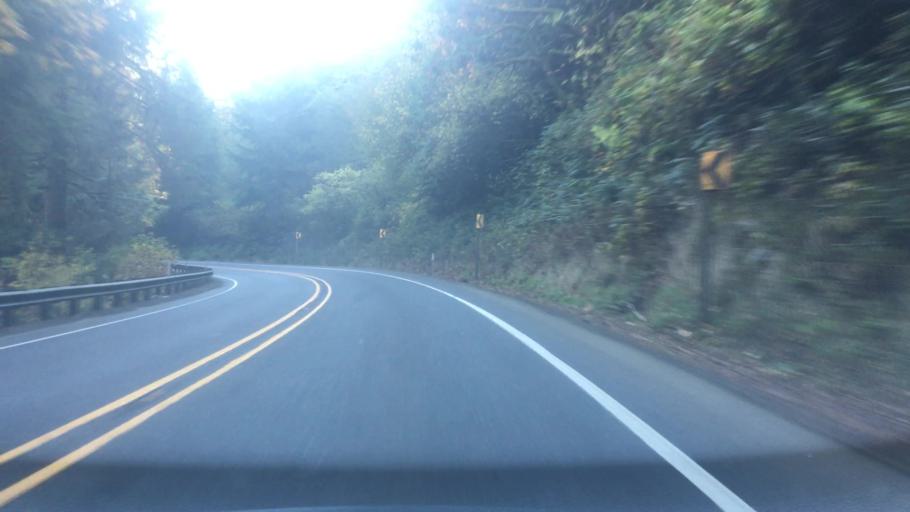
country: US
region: Oregon
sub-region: Lincoln County
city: Rose Lodge
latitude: 45.0072
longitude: -123.9187
